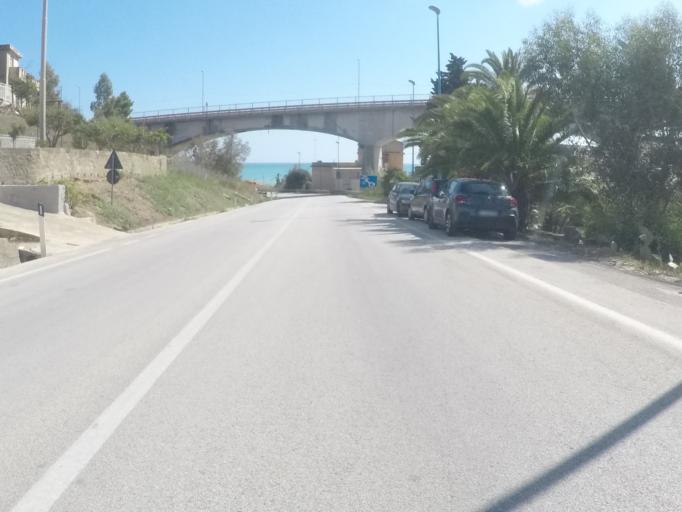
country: IT
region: Sicily
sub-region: Agrigento
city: Porto Empedocle
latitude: 37.2951
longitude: 13.5015
